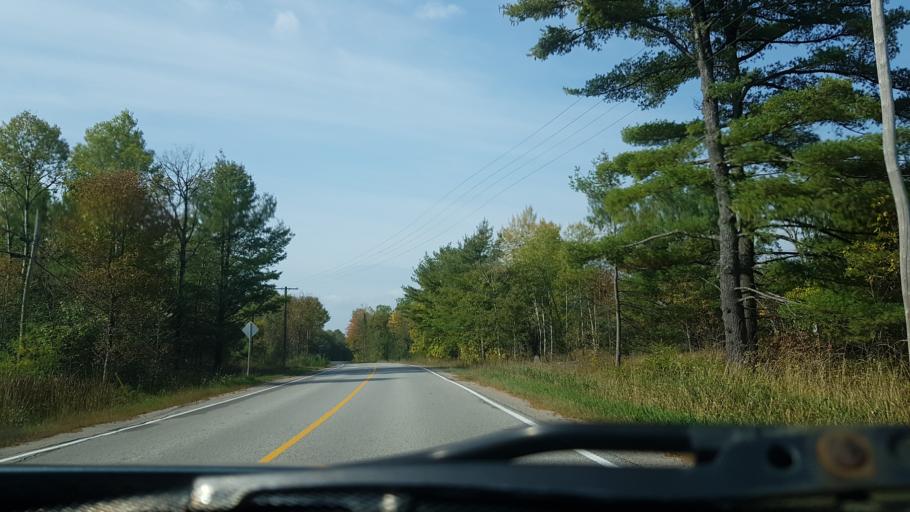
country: CA
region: Ontario
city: Gravenhurst
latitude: 44.7677
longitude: -79.3192
